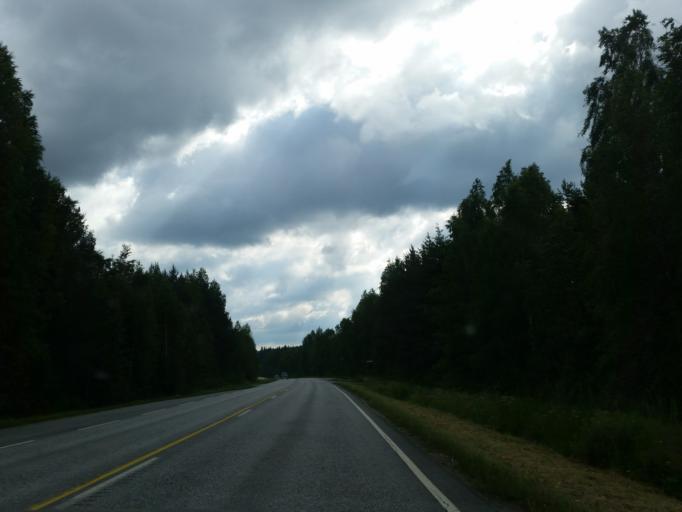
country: FI
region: Northern Savo
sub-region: Kuopio
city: Karttula
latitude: 62.8577
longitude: 27.2156
